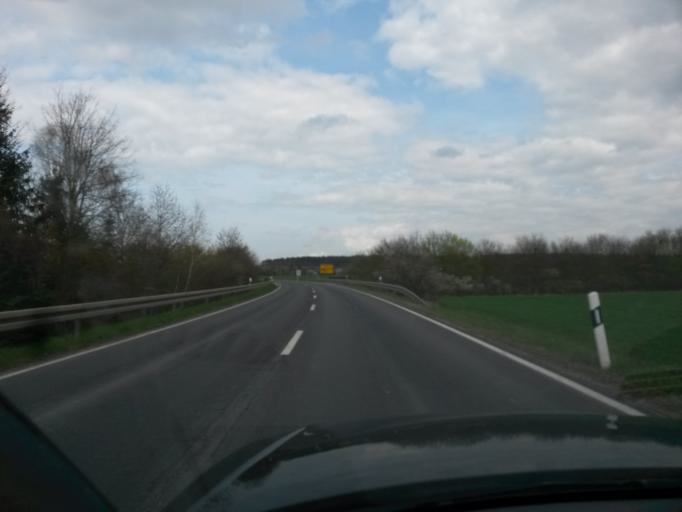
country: DE
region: Bavaria
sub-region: Regierungsbezirk Unterfranken
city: Volkach
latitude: 49.8573
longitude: 10.2392
